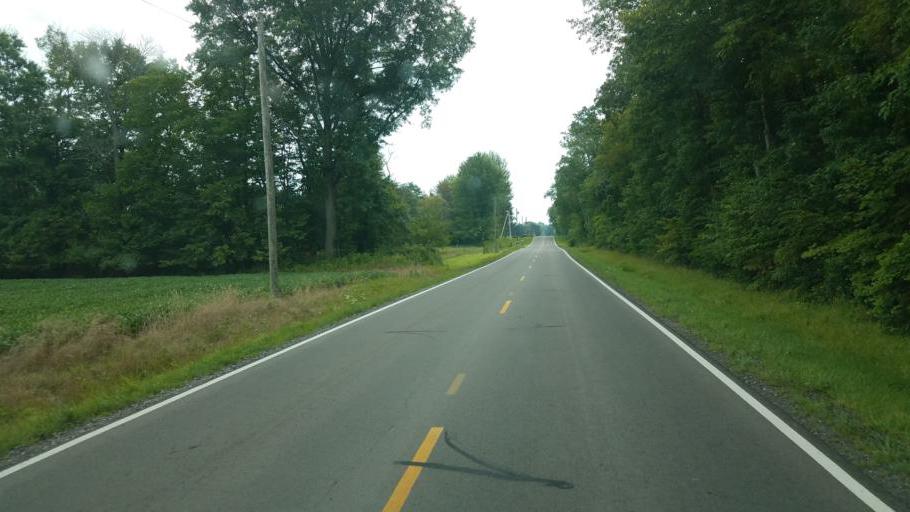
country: US
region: Ohio
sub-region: Crawford County
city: Galion
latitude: 40.7197
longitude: -82.8426
